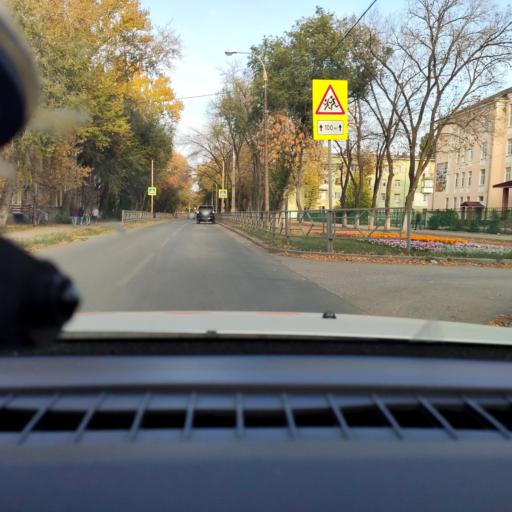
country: RU
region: Samara
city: Samara
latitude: 53.1167
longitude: 50.0808
